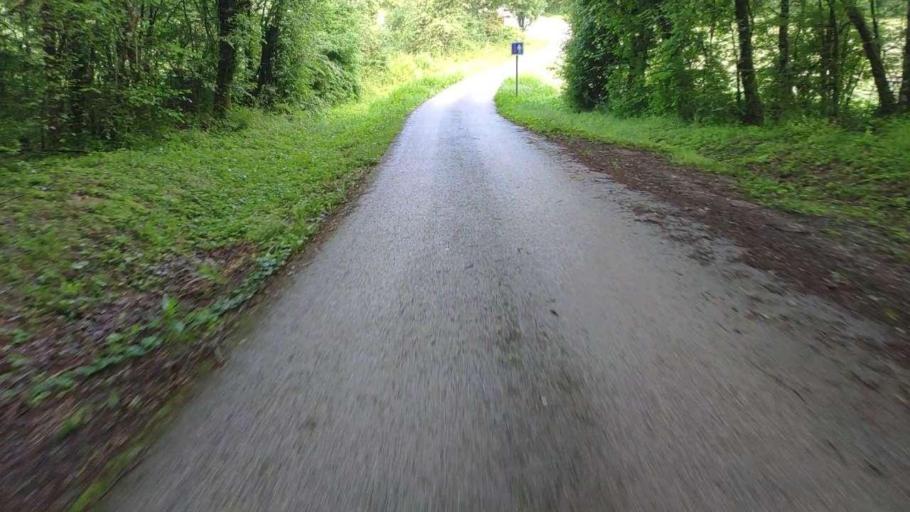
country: FR
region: Franche-Comte
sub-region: Departement du Jura
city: Poligny
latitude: 46.7990
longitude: 5.5978
